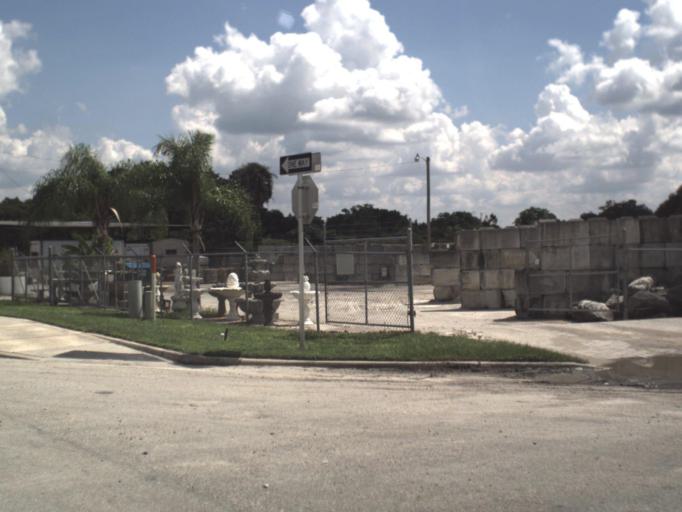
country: US
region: Florida
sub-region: Lee County
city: Tice
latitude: 26.7149
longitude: -81.8233
